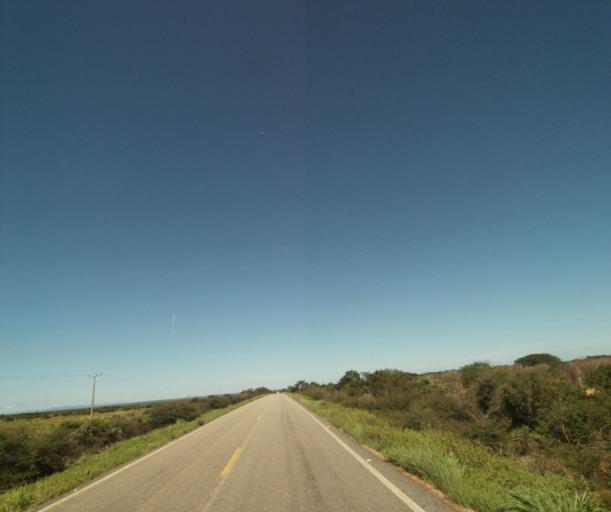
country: BR
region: Bahia
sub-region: Palmas De Monte Alto
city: Palmas de Monte Alto
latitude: -14.2557
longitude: -43.2398
